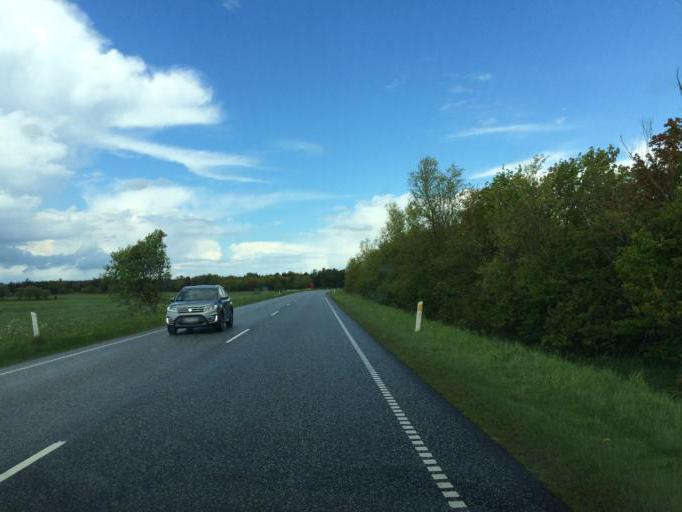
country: DK
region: North Denmark
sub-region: Vesthimmerland Kommune
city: Farso
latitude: 56.6139
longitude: 9.3507
